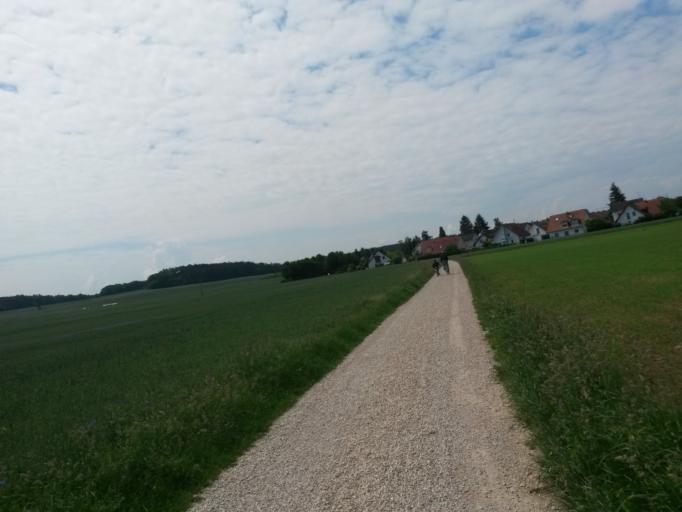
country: DE
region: Bavaria
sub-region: Regierungsbezirk Mittelfranken
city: Rosstal
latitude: 49.4254
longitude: 10.9053
